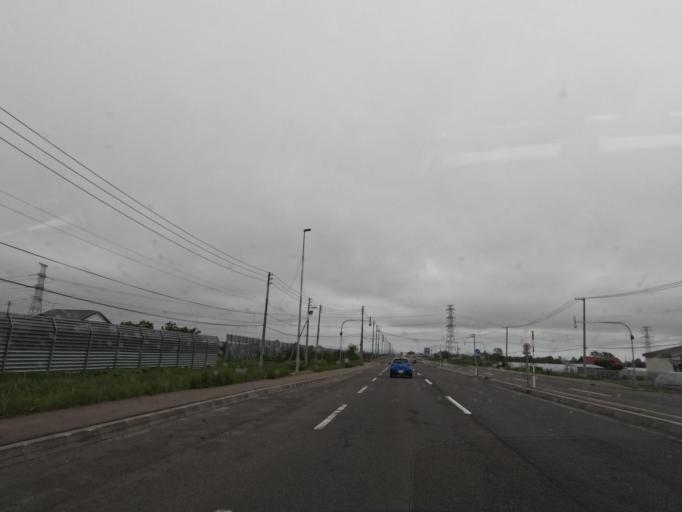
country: JP
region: Hokkaido
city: Tobetsu
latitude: 43.1583
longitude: 141.5190
